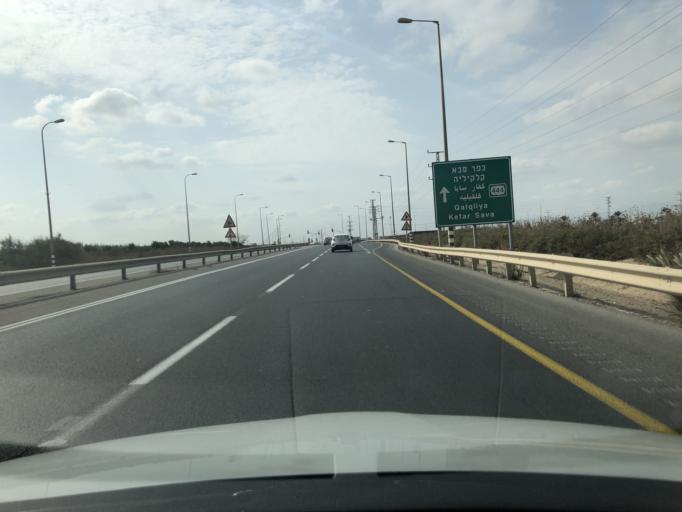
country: IL
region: Central District
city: Tirah
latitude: 32.2341
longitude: 34.9854
